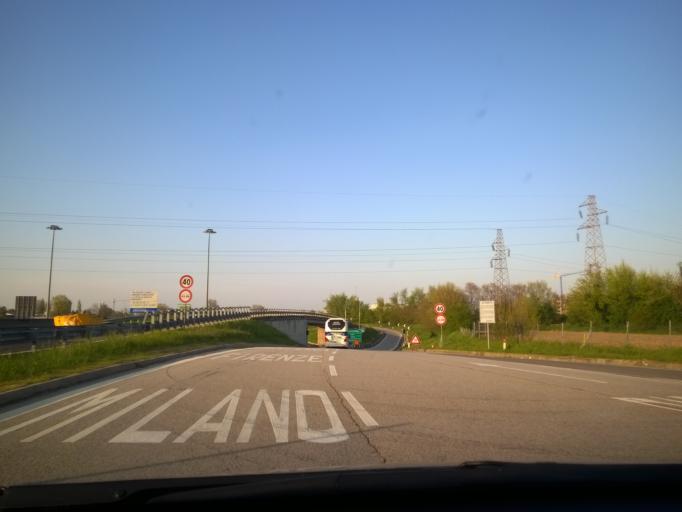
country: IT
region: Emilia-Romagna
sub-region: Provincia di Bologna
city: Progresso
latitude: 44.5313
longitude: 11.3612
